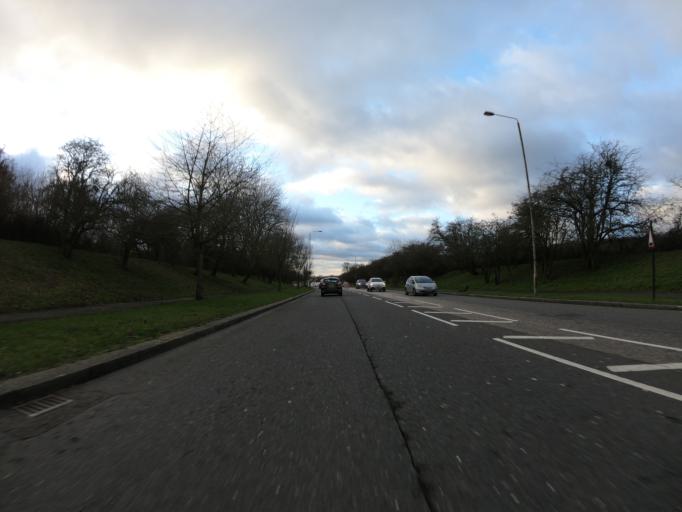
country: GB
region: England
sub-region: Greater London
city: Woolwich
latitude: 51.4626
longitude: 0.0719
